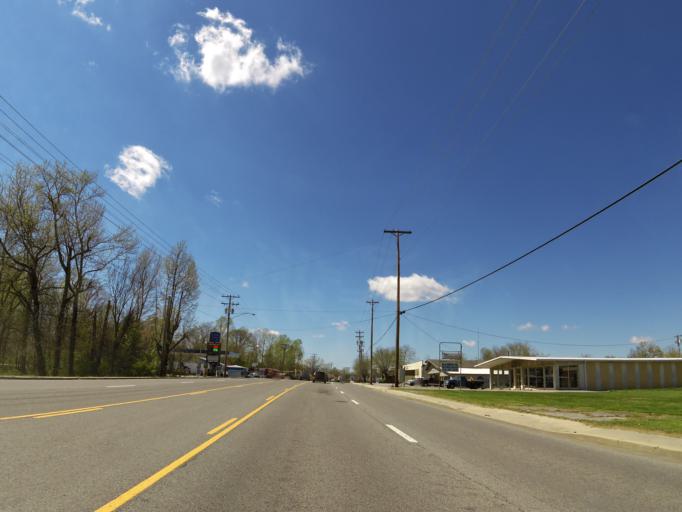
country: US
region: Tennessee
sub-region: DeKalb County
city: Smithville
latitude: 35.9592
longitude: -85.8348
